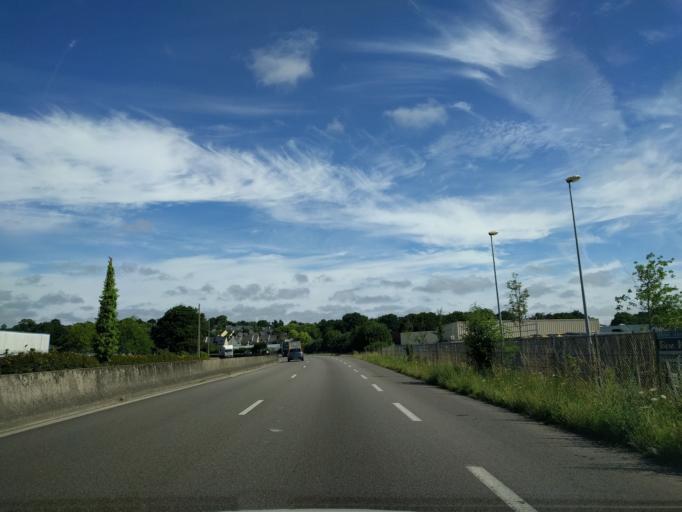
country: FR
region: Brittany
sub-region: Departement du Finistere
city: Quimper
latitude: 47.9968
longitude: -4.0728
